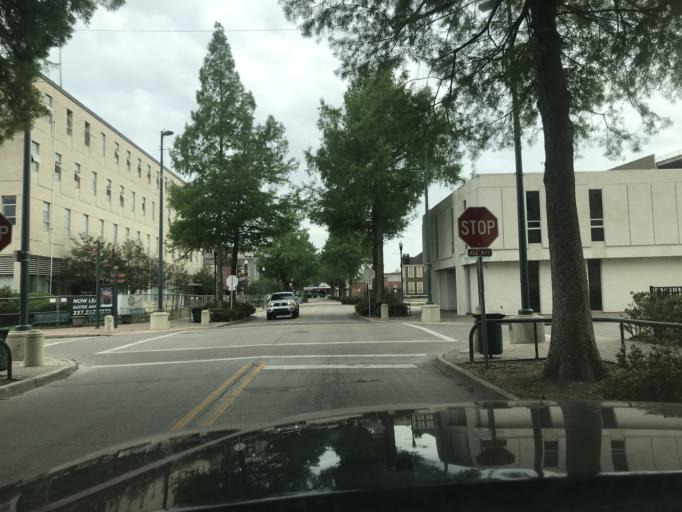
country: US
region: Louisiana
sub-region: Lafayette Parish
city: Lafayette
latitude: 30.2231
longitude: -92.0188
